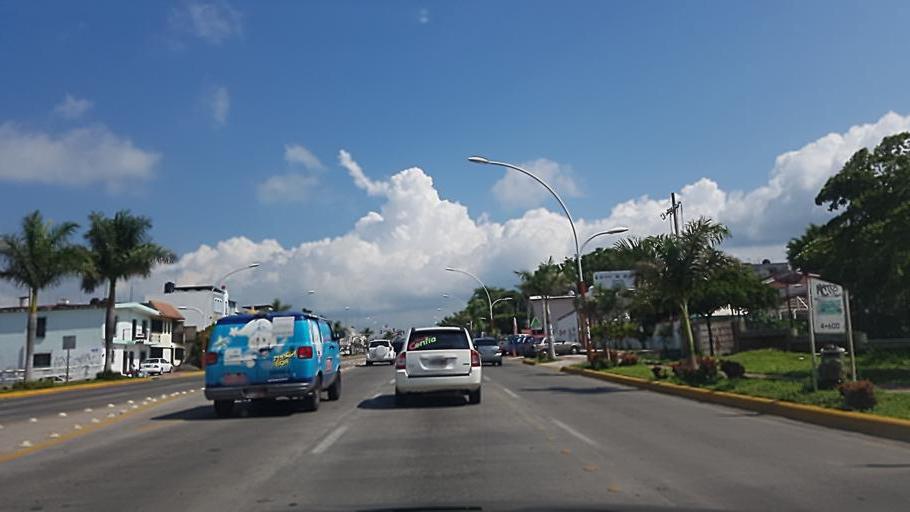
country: MX
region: Nayarit
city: Xalisco
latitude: 21.4777
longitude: -104.8912
